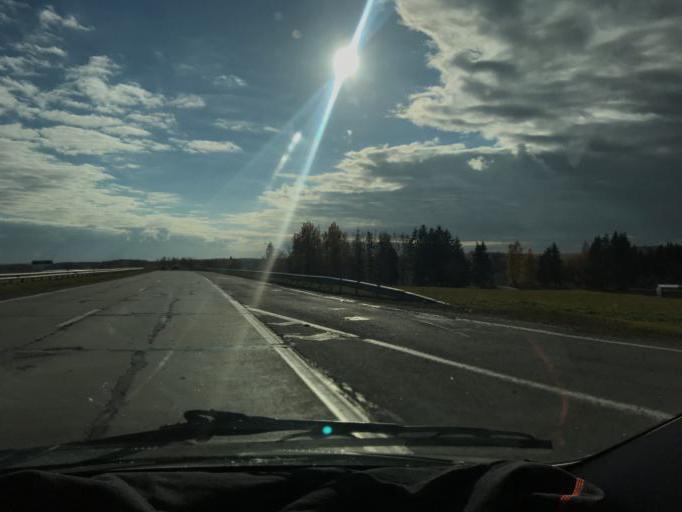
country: BY
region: Minsk
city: Lahoysk
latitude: 54.1587
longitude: 27.8129
